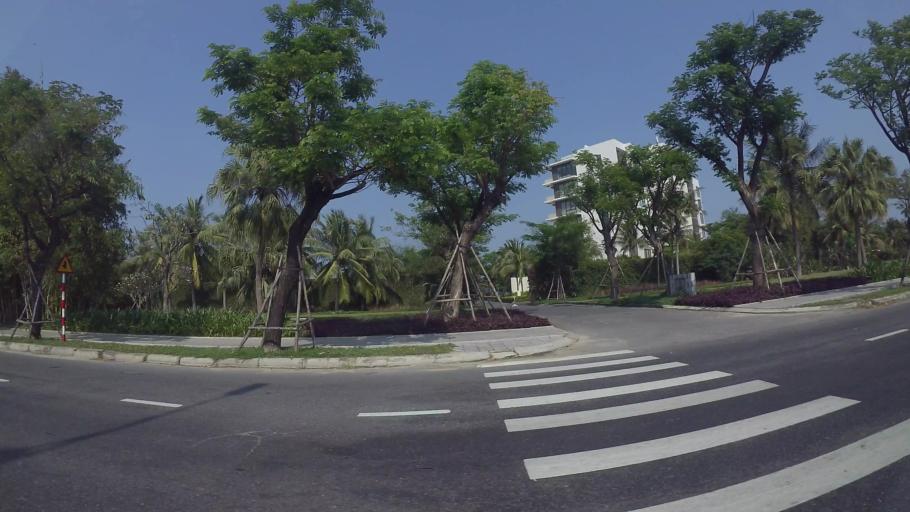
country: VN
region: Da Nang
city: Ngu Hanh Son
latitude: 16.0102
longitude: 108.2634
